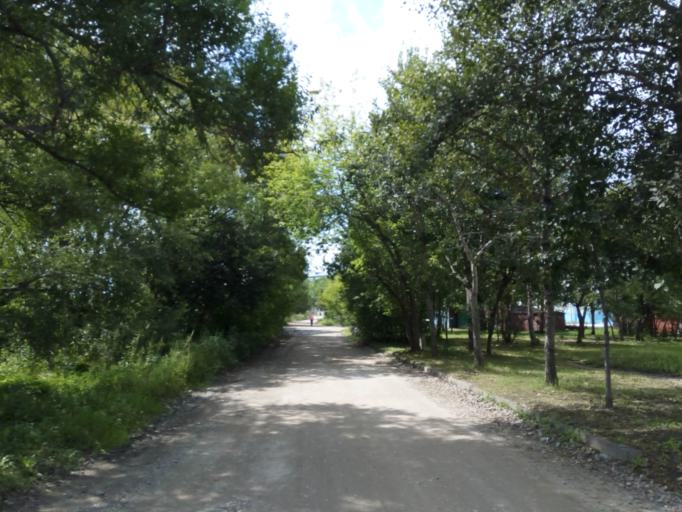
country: RU
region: Primorskiy
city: Dal'nerechensk
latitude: 45.9446
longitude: 133.8179
